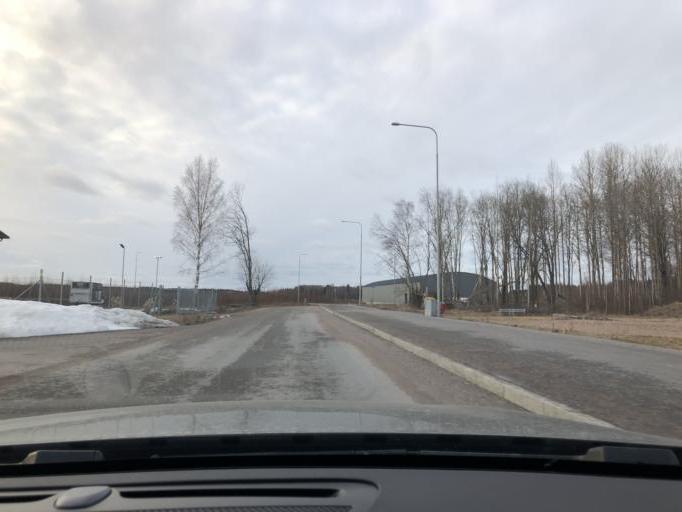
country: SE
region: Uppsala
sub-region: Tierps Kommun
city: Tierp
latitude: 60.3491
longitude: 17.4964
